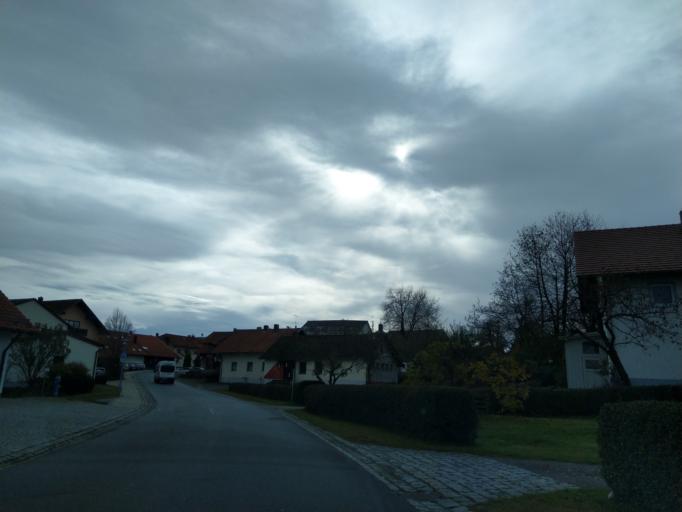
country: DE
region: Bavaria
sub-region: Lower Bavaria
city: Schofweg
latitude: 48.8410
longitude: 13.2276
